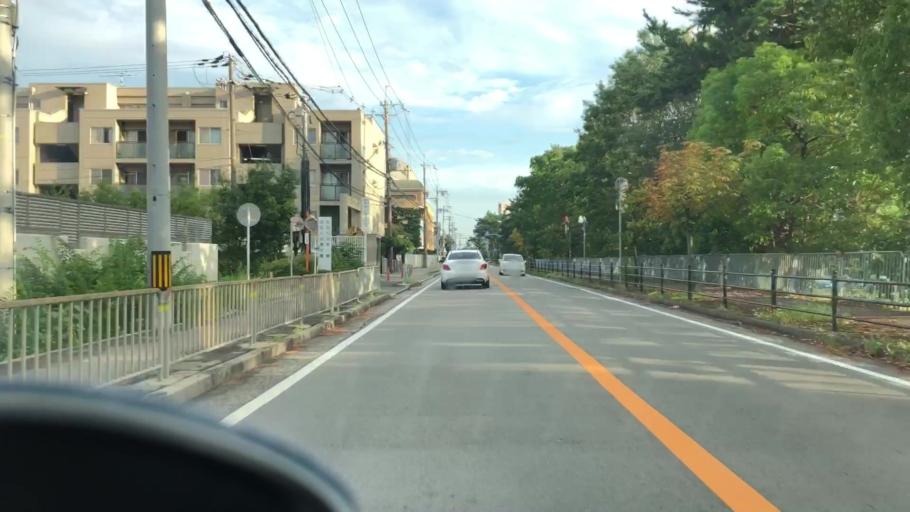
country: JP
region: Hyogo
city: Takarazuka
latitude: 34.7786
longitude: 135.3711
